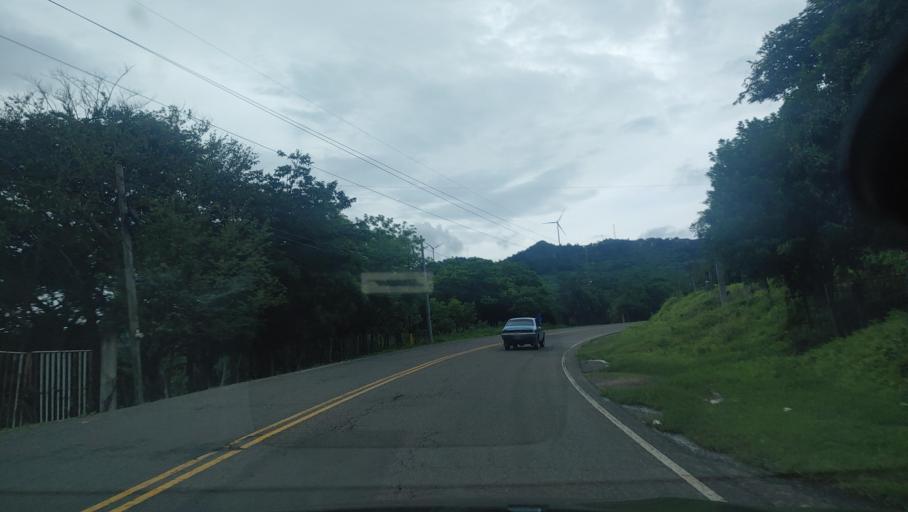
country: HN
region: Choluteca
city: Corpus
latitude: 13.3655
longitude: -86.9780
